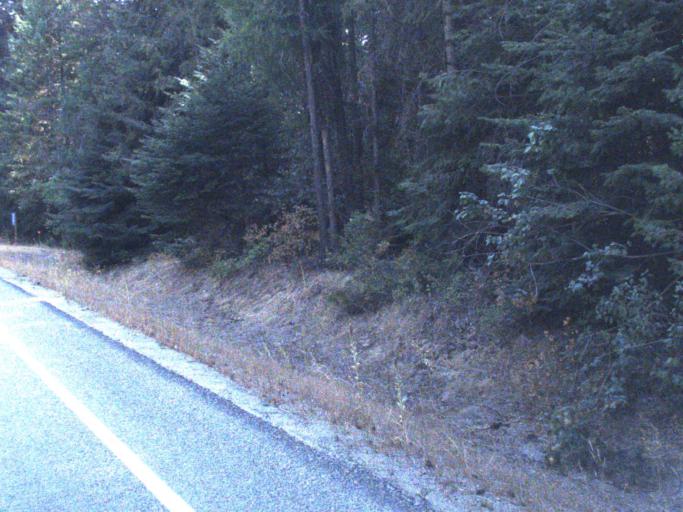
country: US
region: Washington
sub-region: Pend Oreille County
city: Newport
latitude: 48.1590
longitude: -117.3023
